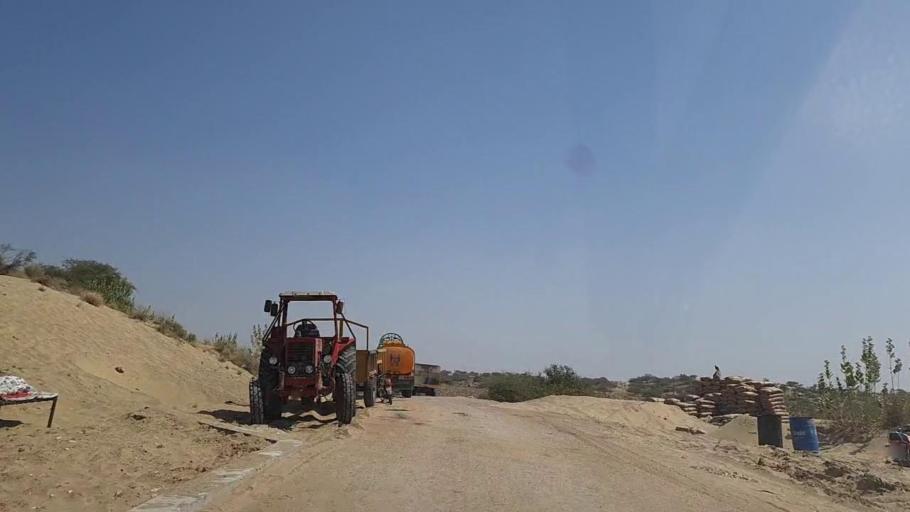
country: PK
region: Sindh
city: Diplo
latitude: 24.4778
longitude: 69.5069
